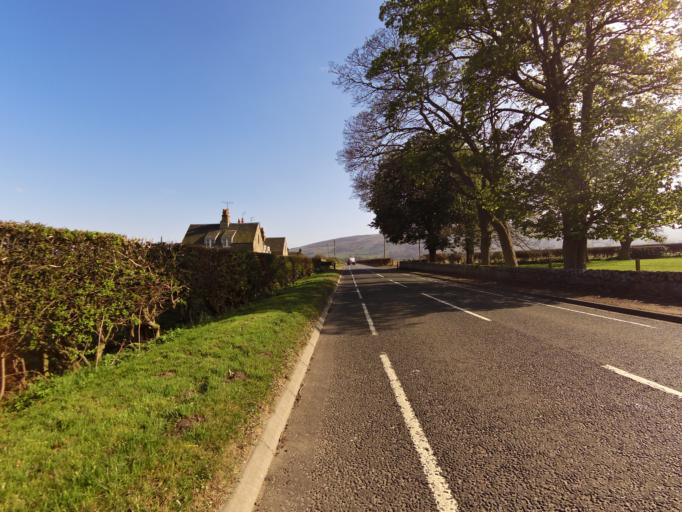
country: GB
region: Scotland
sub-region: Fife
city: Falkland
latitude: 56.2649
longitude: -3.2090
